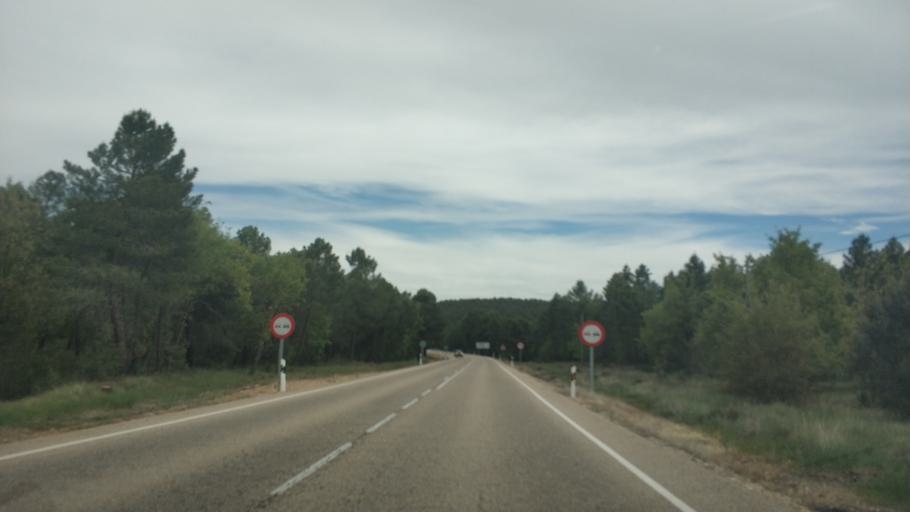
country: ES
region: Castille and Leon
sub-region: Provincia de Soria
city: Bayubas de Abajo
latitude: 41.5145
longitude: -2.9272
